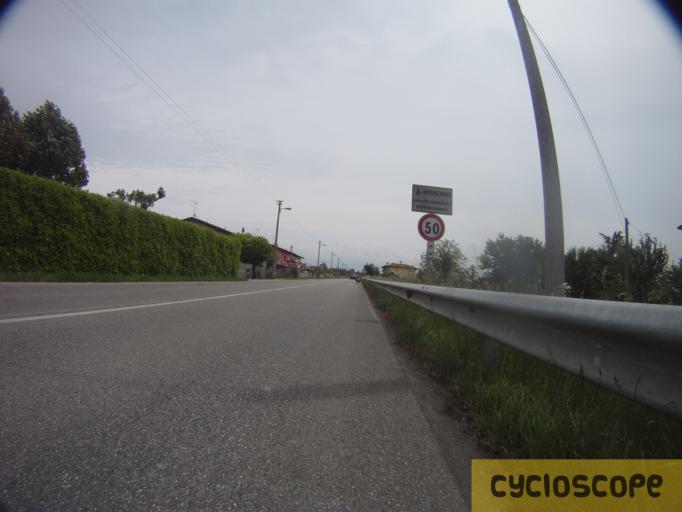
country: IT
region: Friuli Venezia Giulia
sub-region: Provincia di Gorizia
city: Pieris
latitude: 45.8027
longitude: 13.4495
